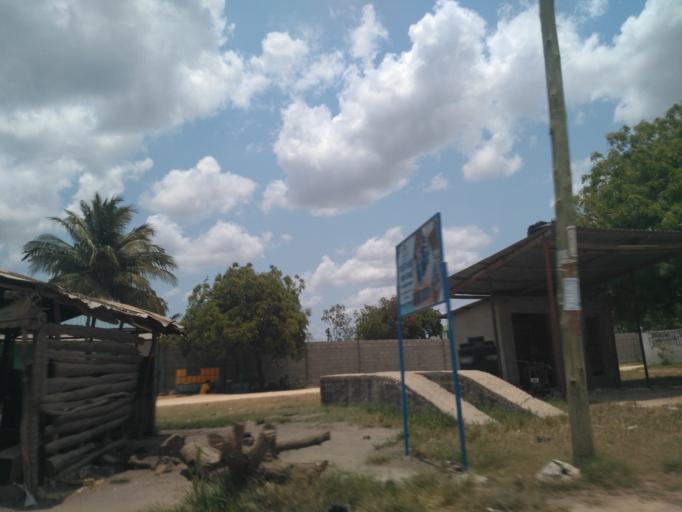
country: TZ
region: Dar es Salaam
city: Dar es Salaam
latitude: -6.8397
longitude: 39.3283
